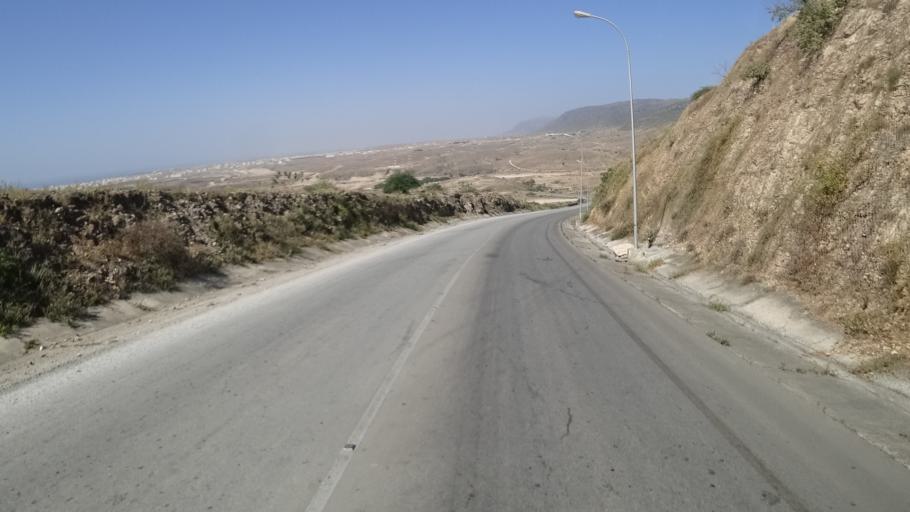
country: OM
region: Zufar
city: Salalah
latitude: 17.0650
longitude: 54.4442
